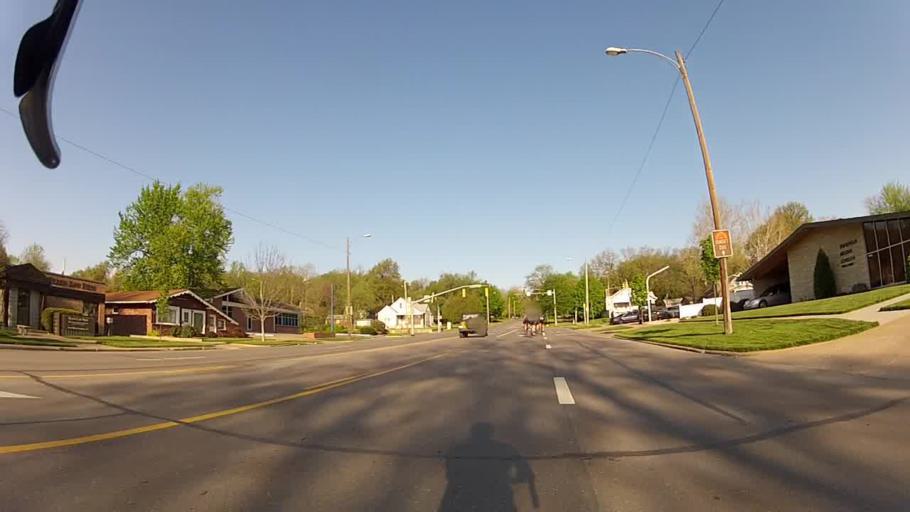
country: US
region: Kansas
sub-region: Riley County
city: Manhattan
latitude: 39.1796
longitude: -96.5824
